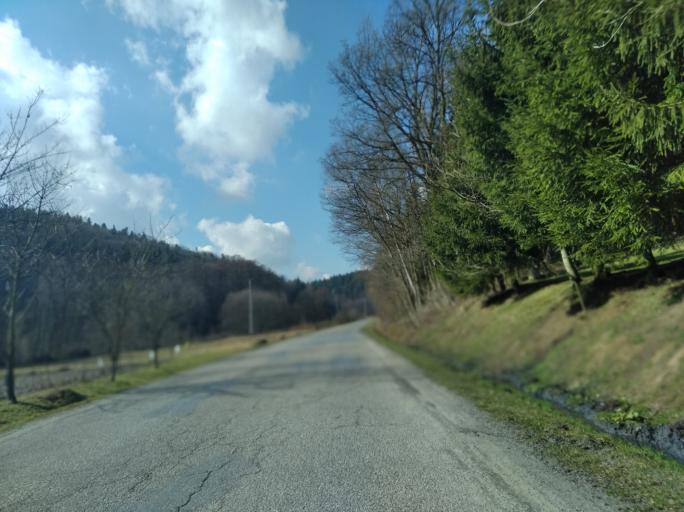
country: PL
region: Subcarpathian Voivodeship
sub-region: Powiat strzyzowski
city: Frysztak
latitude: 49.8662
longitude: 21.5592
